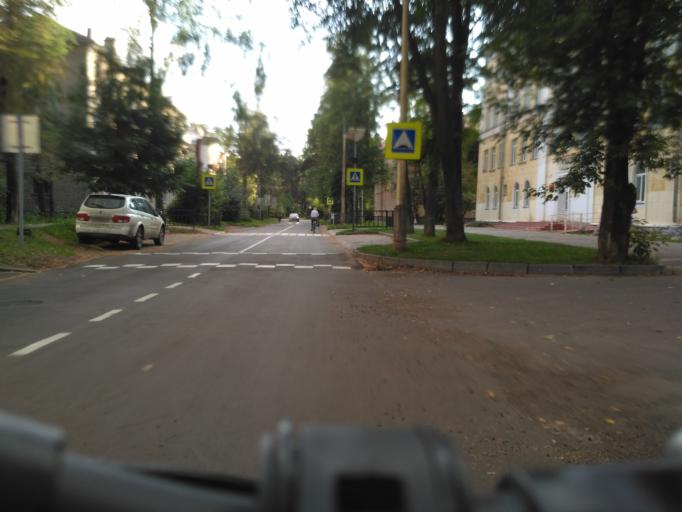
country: RU
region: Moskovskaya
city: Dubna
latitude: 56.7493
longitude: 37.1950
